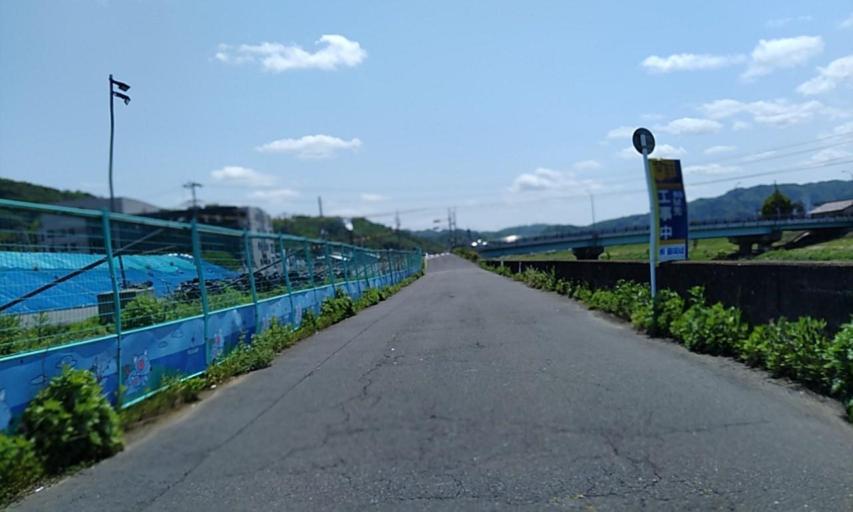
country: JP
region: Kyoto
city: Maizuru
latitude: 35.4461
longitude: 135.3364
